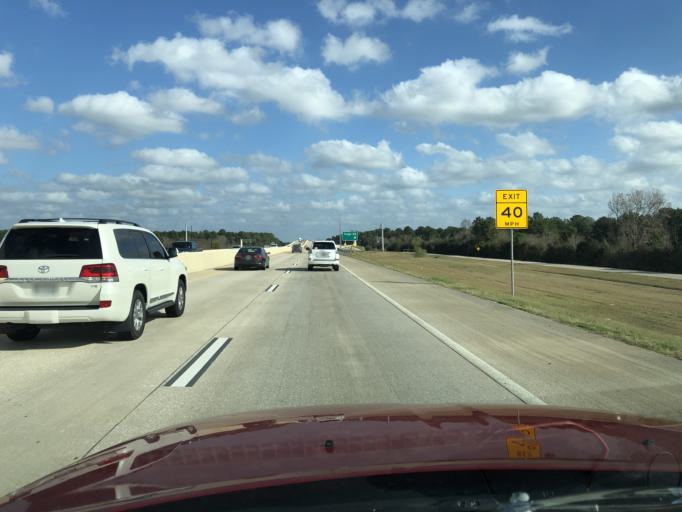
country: US
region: Texas
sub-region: Harris County
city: Tomball
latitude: 30.0502
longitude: -95.6679
